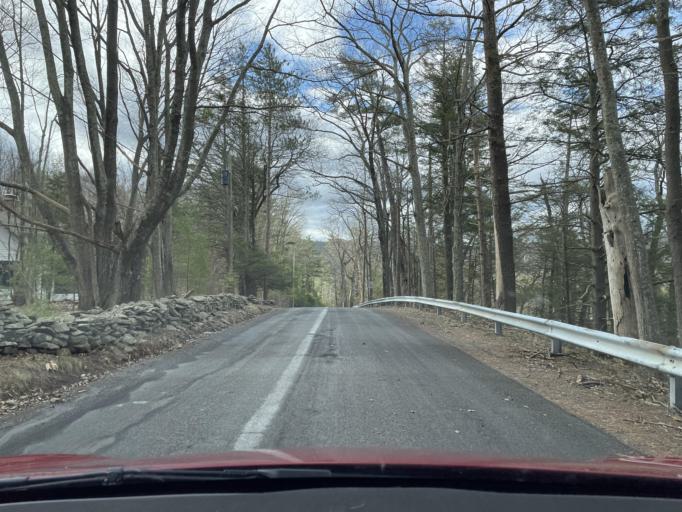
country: US
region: New York
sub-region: Ulster County
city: Woodstock
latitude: 42.0454
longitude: -74.1551
